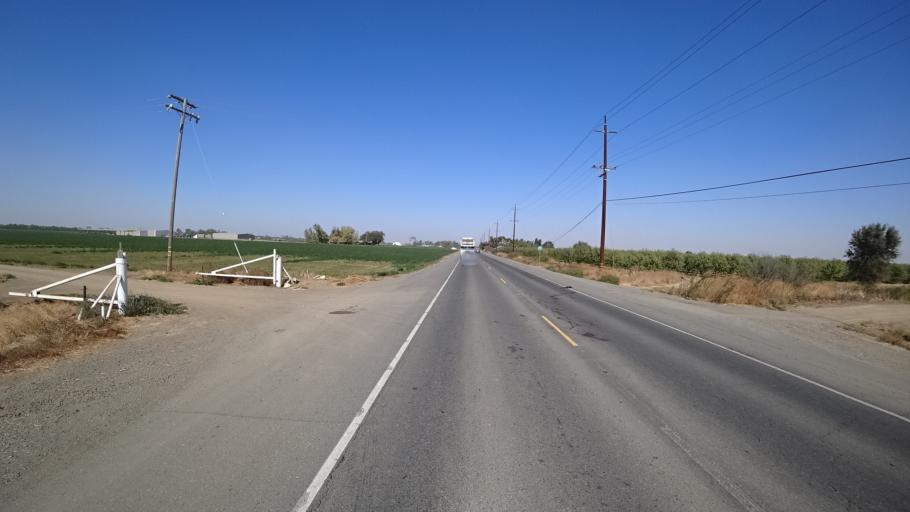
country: US
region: California
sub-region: Yolo County
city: Davis
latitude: 38.6043
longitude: -121.7301
